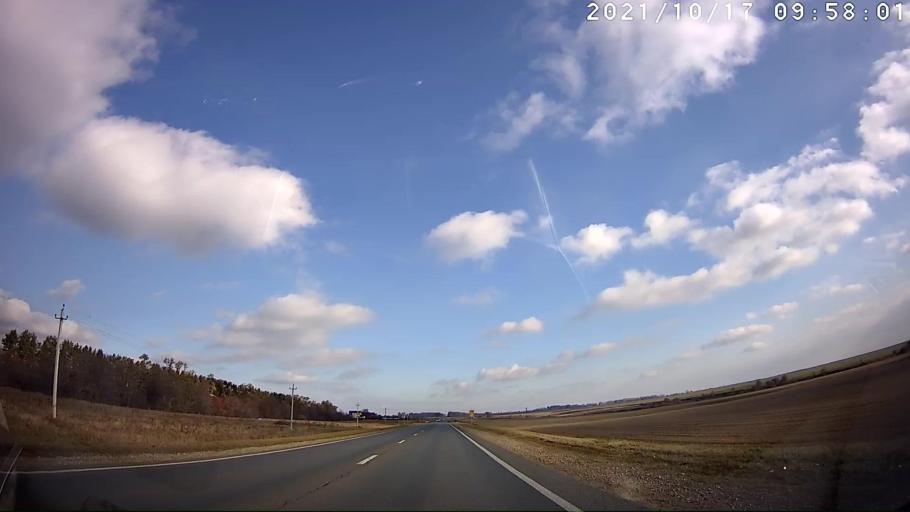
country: RU
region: Mariy-El
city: Yoshkar-Ola
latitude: 56.7036
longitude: 48.0726
